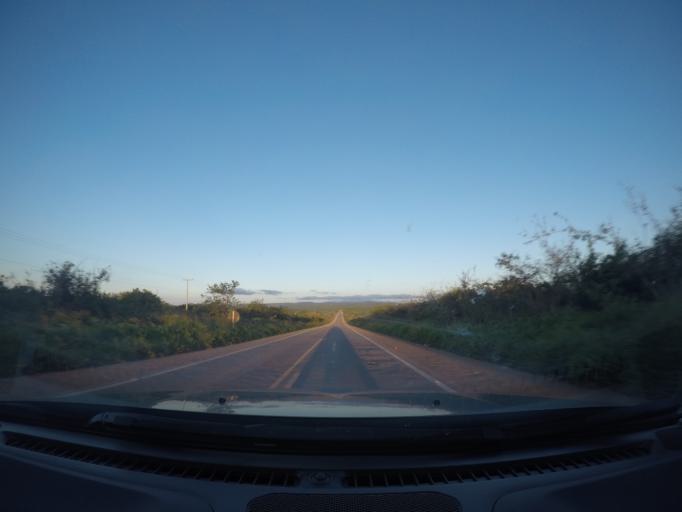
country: BR
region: Bahia
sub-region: Seabra
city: Seabra
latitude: -12.4014
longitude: -41.9463
